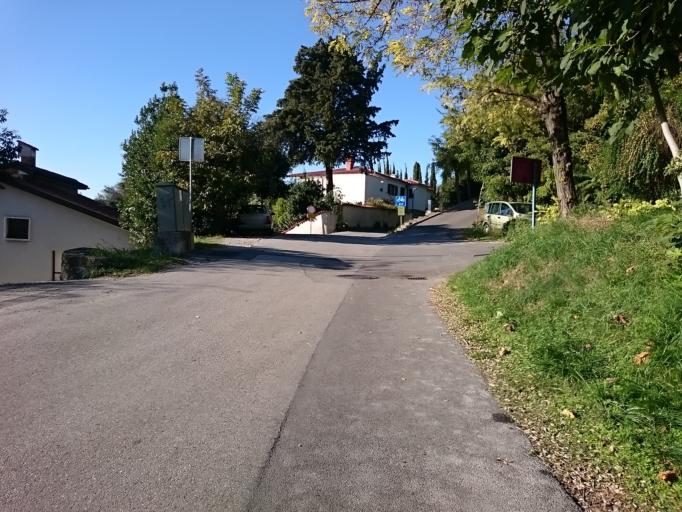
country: SI
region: Piran-Pirano
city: Portoroz
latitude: 45.5125
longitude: 13.5972
